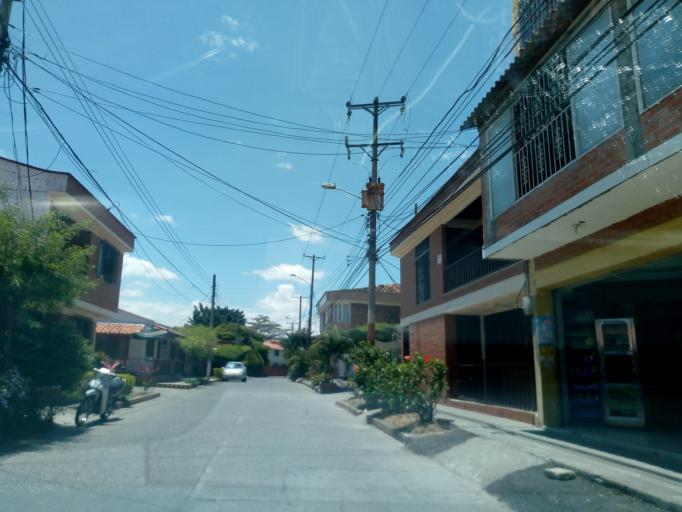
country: CO
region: Valle del Cauca
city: Cartago
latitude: 4.7361
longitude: -75.9123
